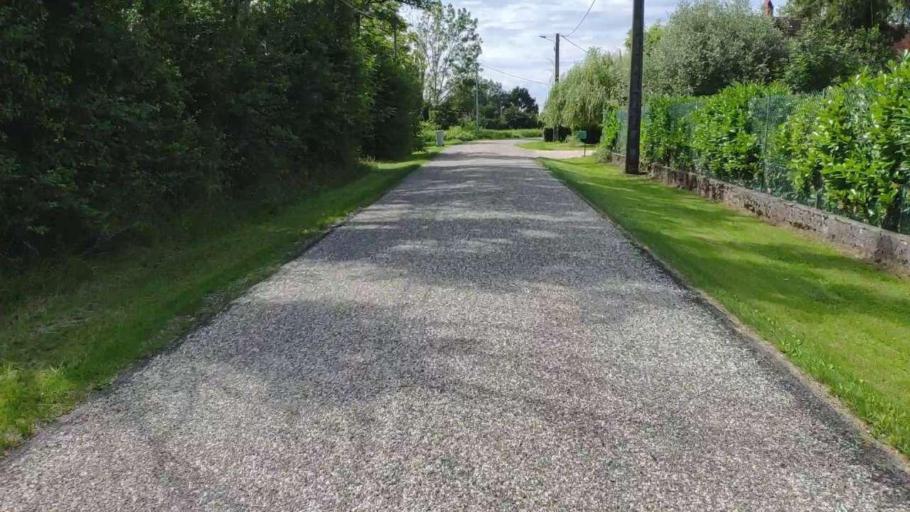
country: FR
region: Franche-Comte
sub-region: Departement du Jura
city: Bletterans
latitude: 46.8194
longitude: 5.4513
